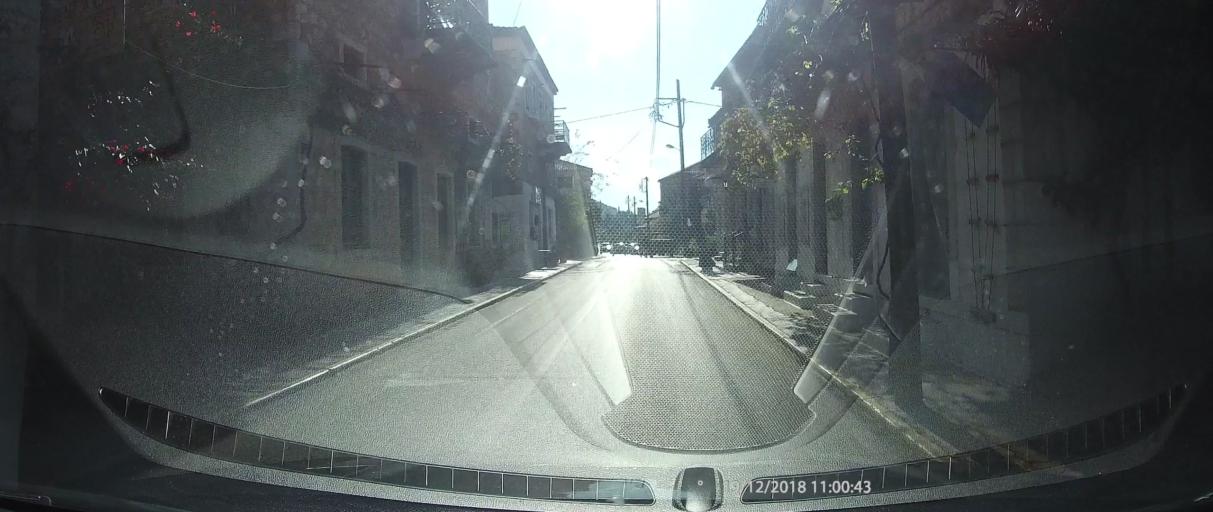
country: GR
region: Peloponnese
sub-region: Nomos Messinias
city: Kardamyli
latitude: 36.8876
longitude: 22.2327
